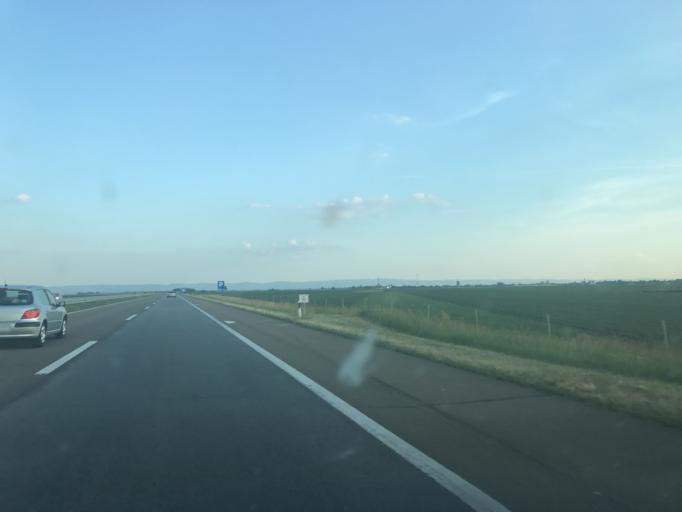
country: RS
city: Kisac
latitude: 45.3772
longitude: 19.7476
